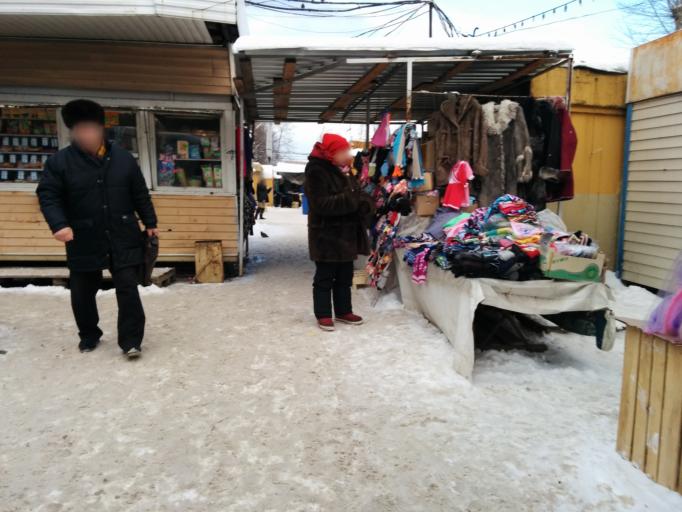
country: RU
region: Perm
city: Perm
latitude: 57.9826
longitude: 56.2922
